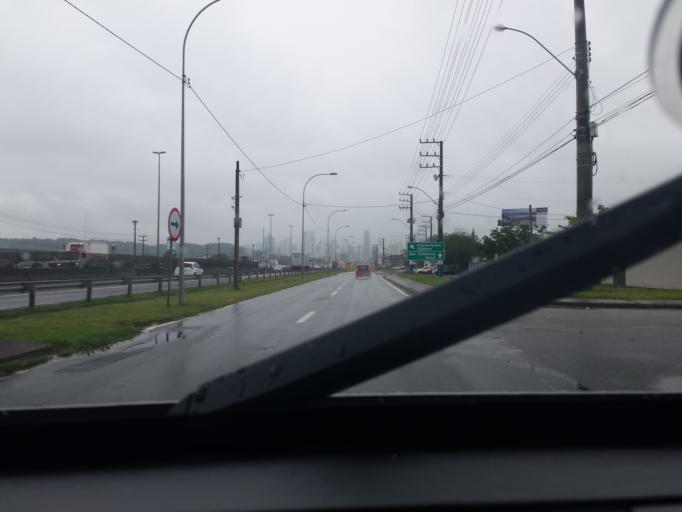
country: BR
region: Santa Catarina
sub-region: Balneario Camboriu
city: Balneario Camboriu
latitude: -27.0238
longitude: -48.6074
